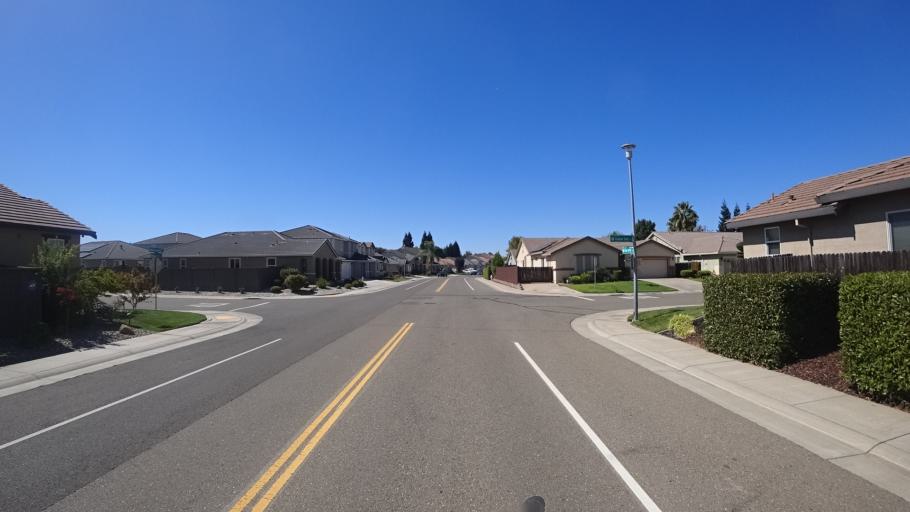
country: US
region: California
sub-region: Sacramento County
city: Elk Grove
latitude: 38.4182
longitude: -121.3380
